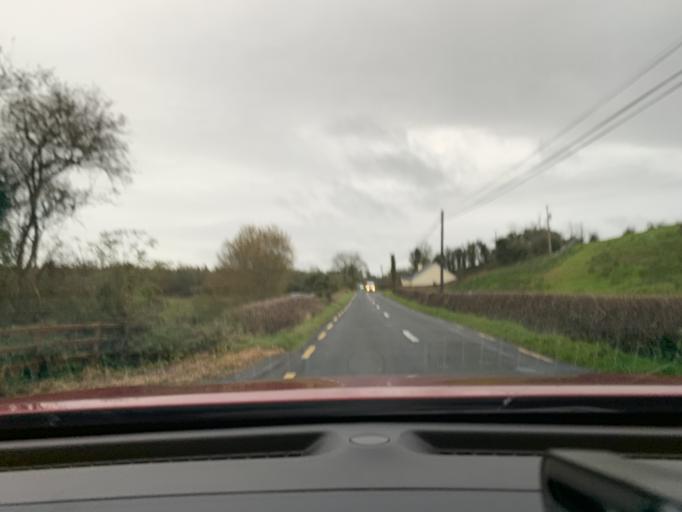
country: IE
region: Connaught
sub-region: Sligo
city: Ballymote
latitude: 54.0450
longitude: -8.5230
